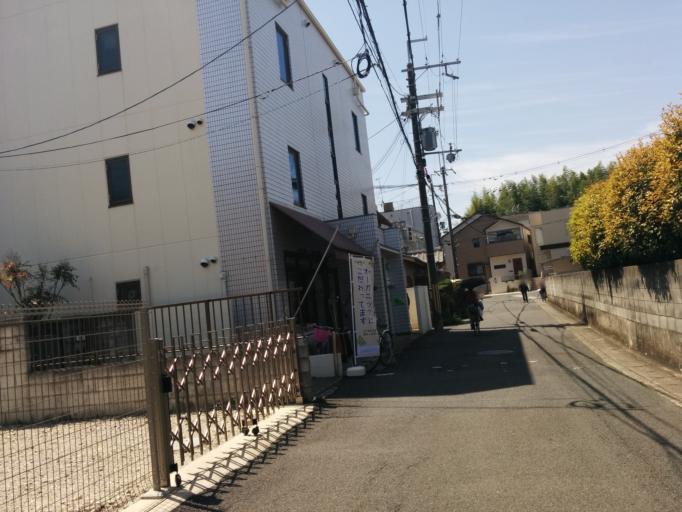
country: JP
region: Kyoto
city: Muko
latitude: 34.9547
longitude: 135.7039
